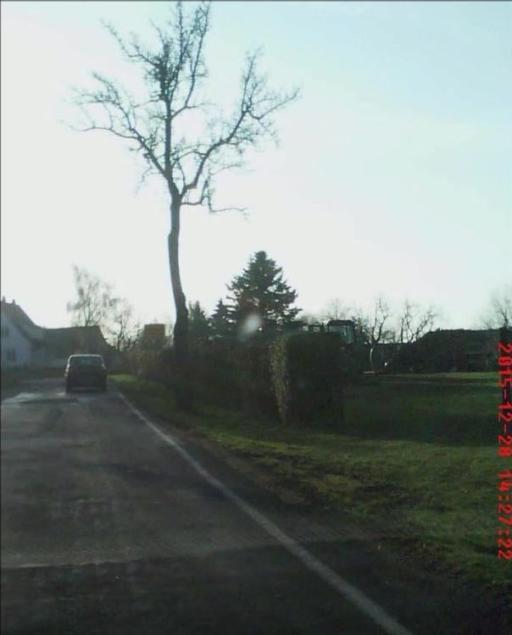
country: DE
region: Thuringia
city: Liebstedt
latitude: 51.0503
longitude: 11.4137
